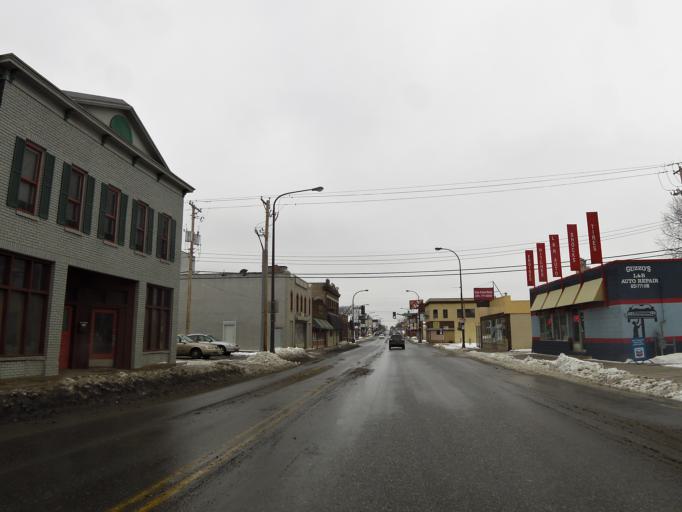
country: US
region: Minnesota
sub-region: Ramsey County
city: Saint Paul
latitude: 44.9695
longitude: -93.0660
